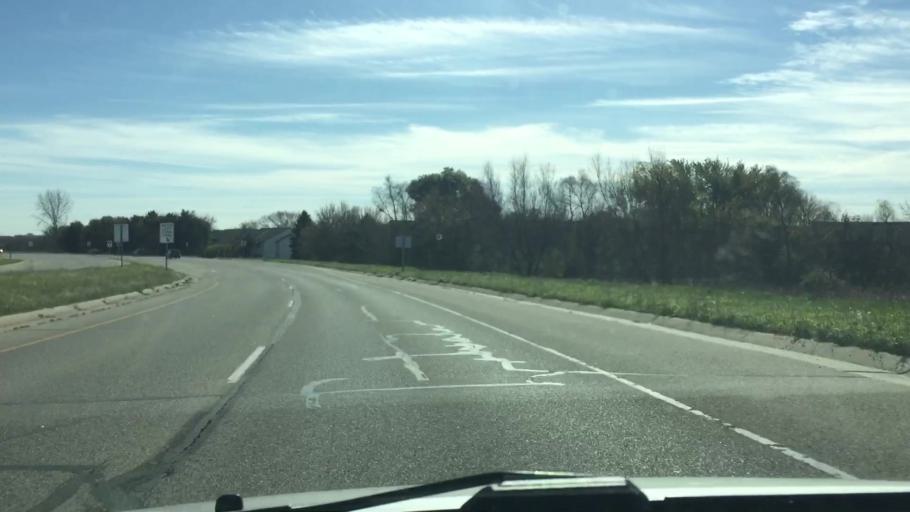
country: US
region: Wisconsin
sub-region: Waukesha County
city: Pewaukee
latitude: 43.0957
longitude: -88.2433
